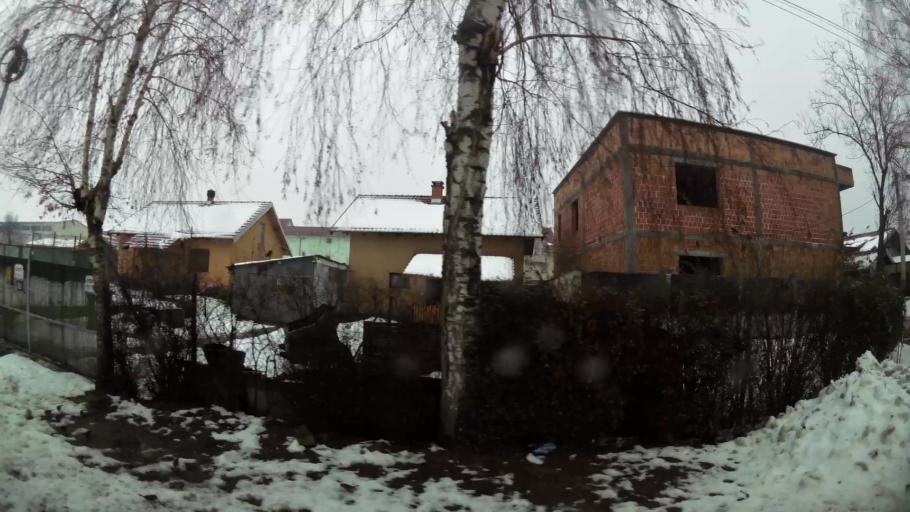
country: RS
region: Central Serbia
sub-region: Belgrade
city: Zemun
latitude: 44.8569
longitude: 20.3573
